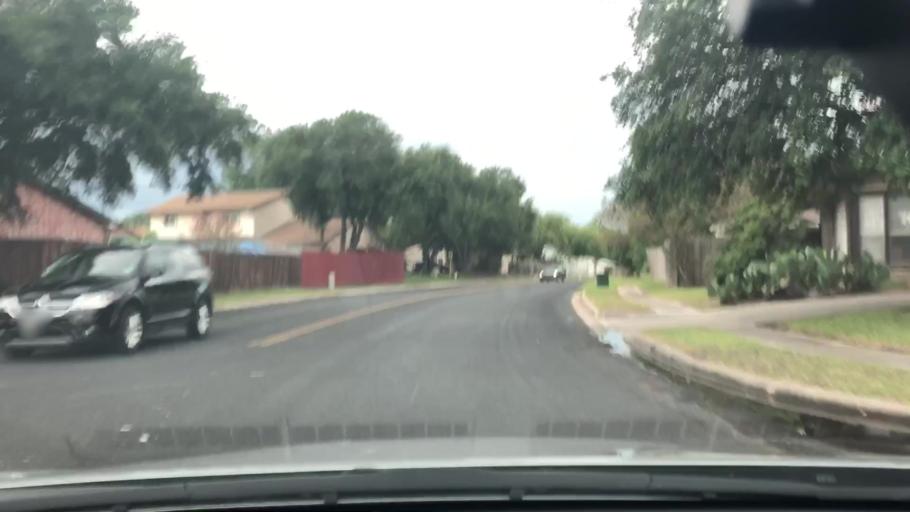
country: US
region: Texas
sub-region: Bexar County
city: Kirby
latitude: 29.4760
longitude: -98.3573
